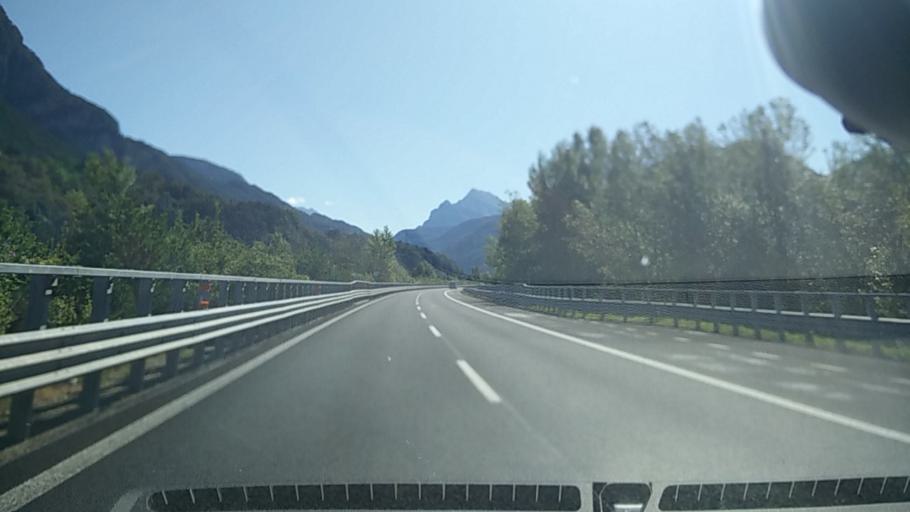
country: IT
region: Friuli Venezia Giulia
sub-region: Provincia di Udine
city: Resiutta
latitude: 46.3972
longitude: 13.2090
